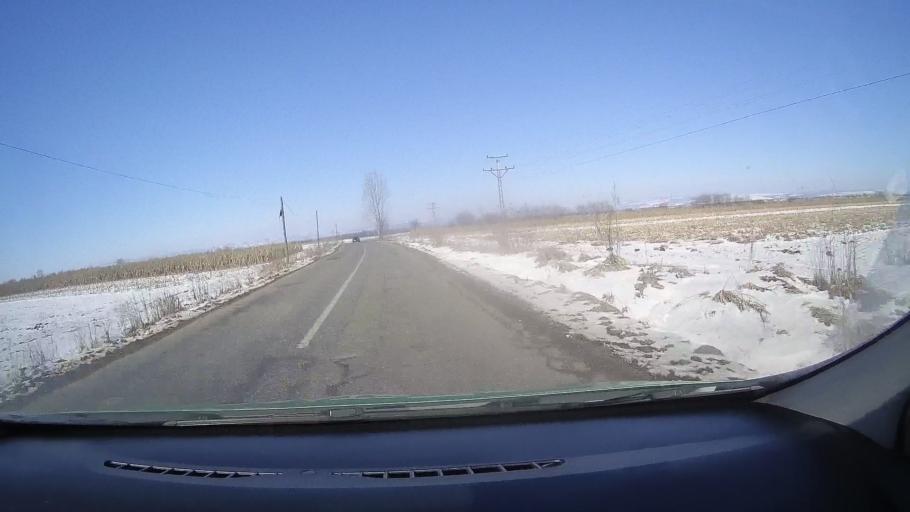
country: RO
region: Brasov
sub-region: Comuna Harseni
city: Harseni
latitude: 45.7645
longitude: 25.0055
